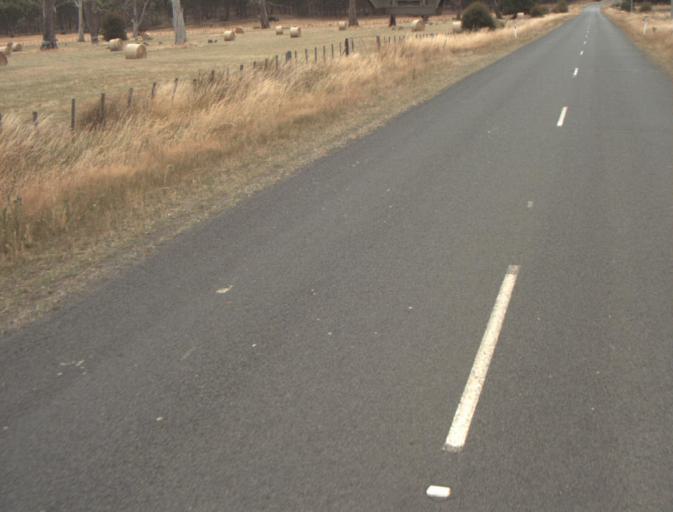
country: AU
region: Tasmania
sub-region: Northern Midlands
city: Evandale
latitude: -41.5030
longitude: 147.4859
